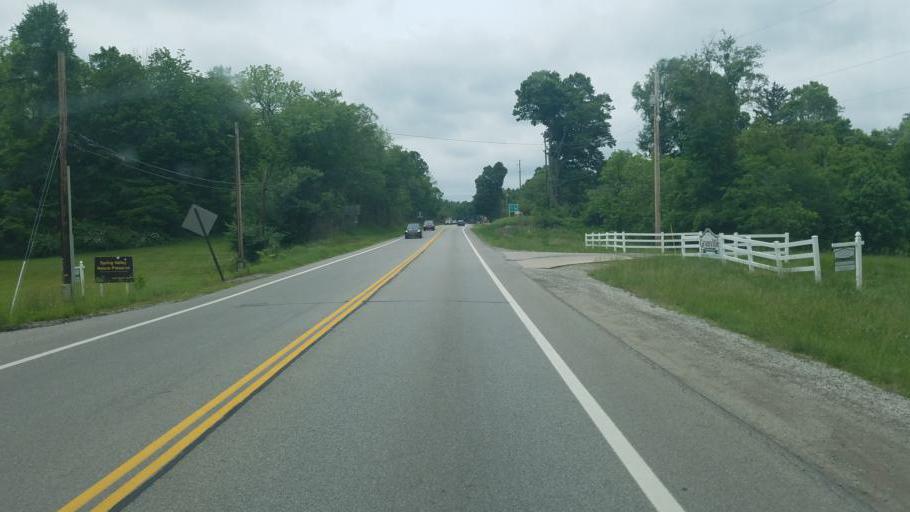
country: US
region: Ohio
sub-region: Licking County
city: Granville
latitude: 40.0600
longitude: -82.5304
